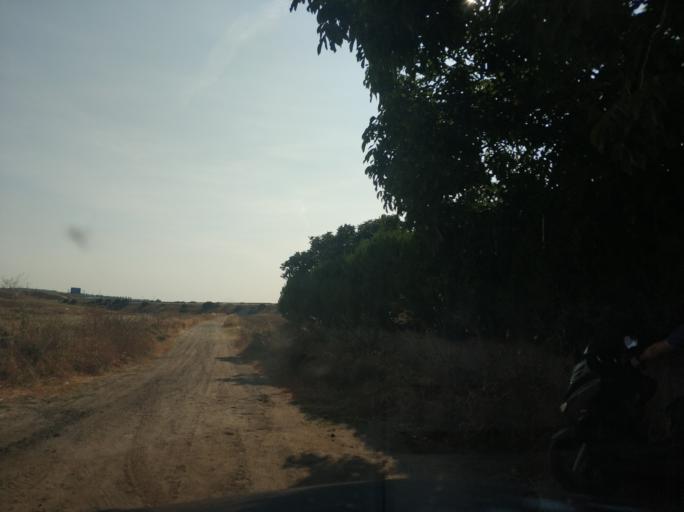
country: ES
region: Castille and Leon
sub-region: Provincia de Salamanca
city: Villamayor
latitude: 41.0103
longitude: -5.6762
